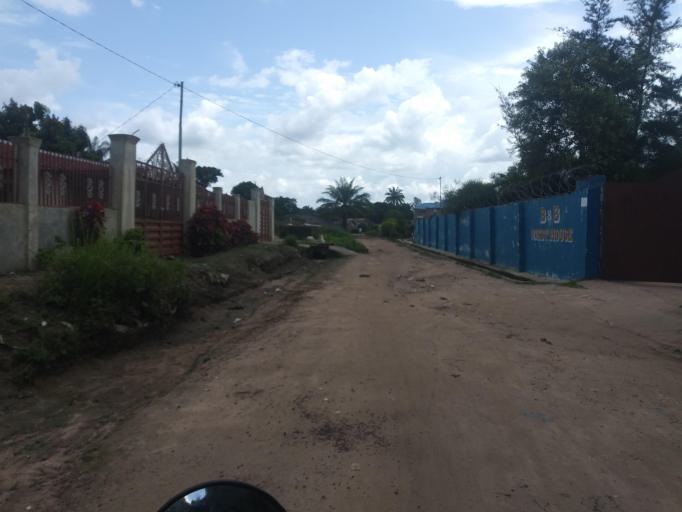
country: SL
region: Northern Province
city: Makeni
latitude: 8.8723
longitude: -12.0427
